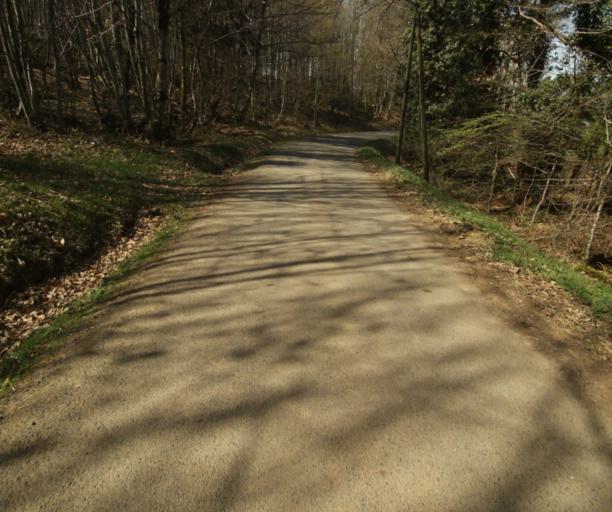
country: FR
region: Limousin
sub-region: Departement de la Correze
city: Naves
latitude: 45.3603
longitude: 1.7777
